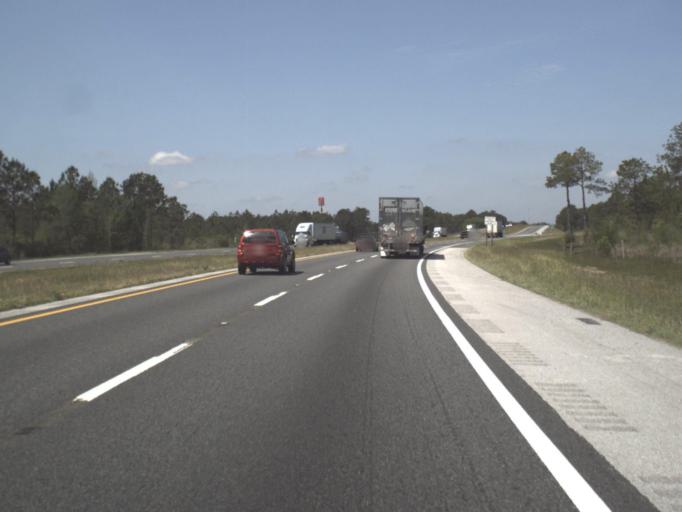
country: US
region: Florida
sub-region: Santa Rosa County
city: Bagdad
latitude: 30.5343
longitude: -87.0797
